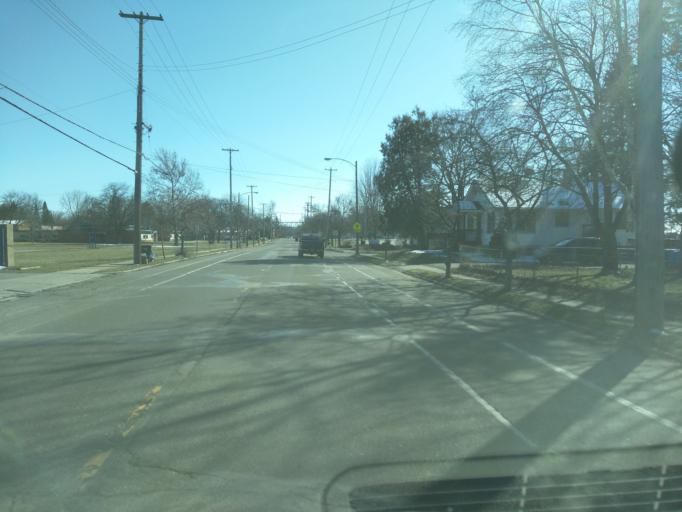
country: US
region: Michigan
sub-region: Ingham County
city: Lansing
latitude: 42.6904
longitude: -84.5823
